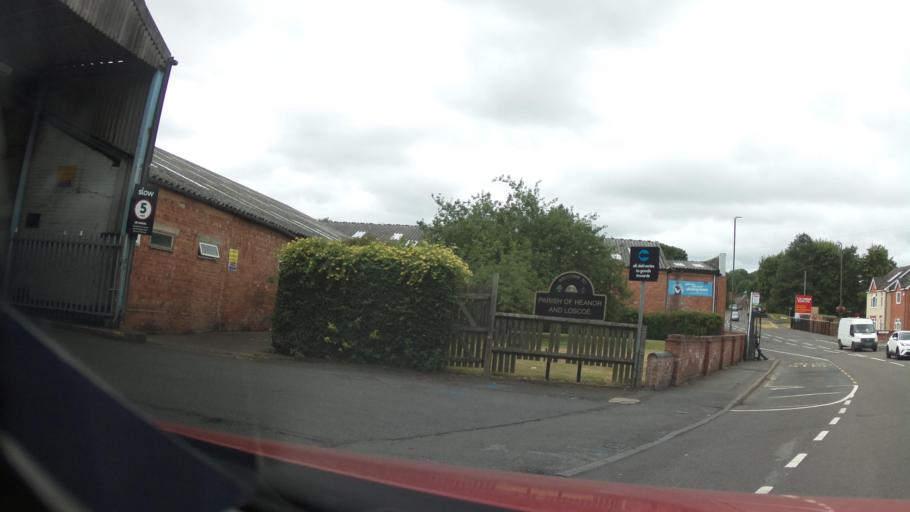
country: GB
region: England
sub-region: Derbyshire
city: Heanor
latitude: 53.0183
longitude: -1.3395
